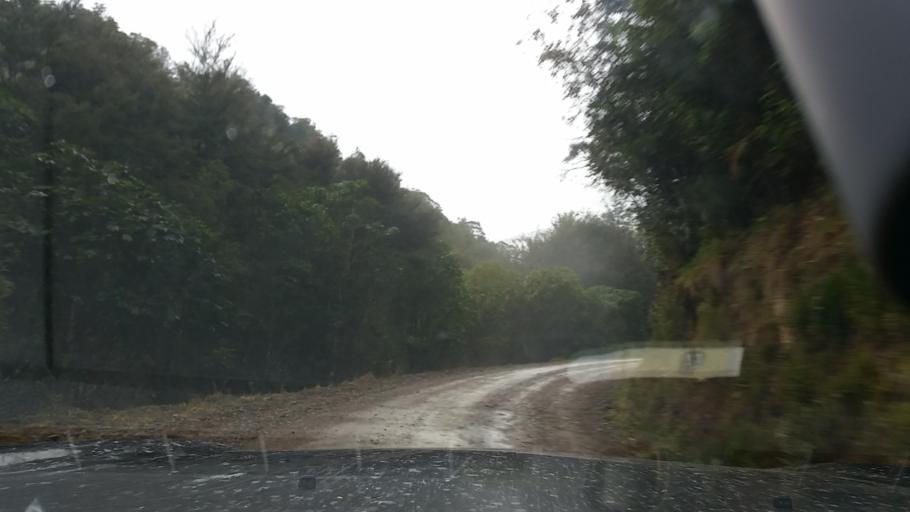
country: NZ
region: Nelson
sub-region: Nelson City
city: Nelson
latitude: -41.3733
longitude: 173.6001
